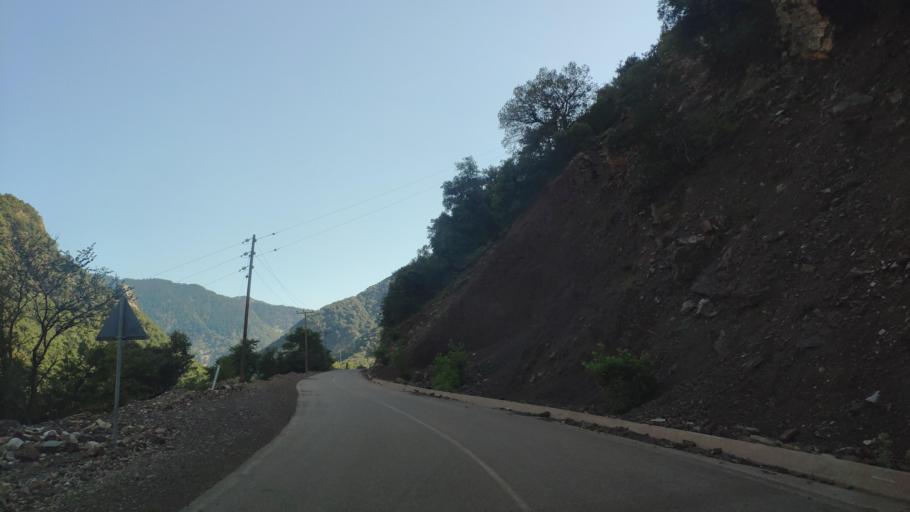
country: GR
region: Central Greece
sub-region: Nomos Evrytanias
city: Kerasochori
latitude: 39.0856
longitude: 21.5961
